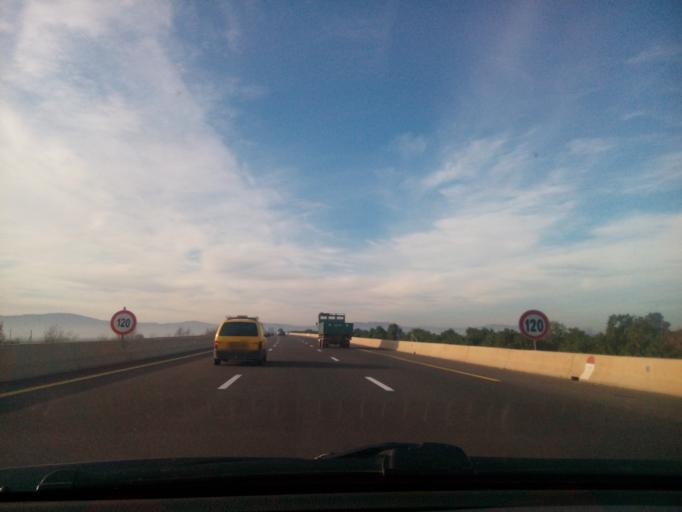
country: DZ
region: Mascara
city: Sig
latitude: 35.6020
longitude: -0.0373
